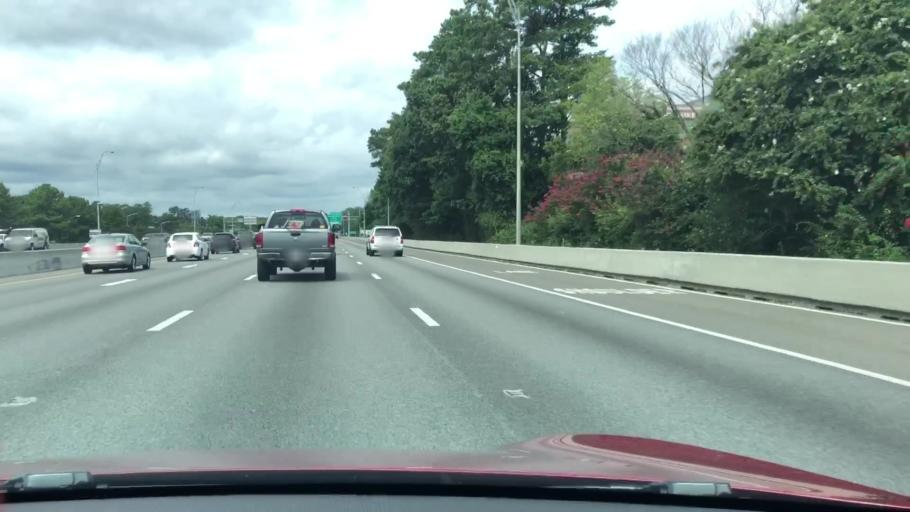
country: US
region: Virginia
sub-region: City of Virginia Beach
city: Virginia Beach
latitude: 36.8323
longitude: -76.1234
